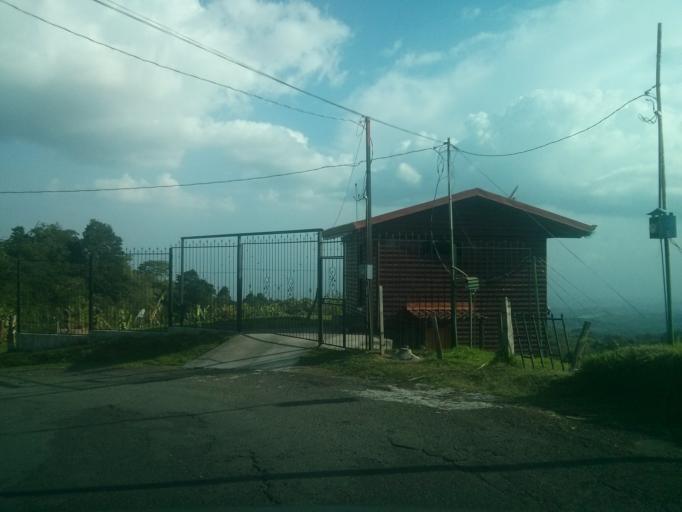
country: CR
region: Heredia
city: Santo Domingo
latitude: 10.1130
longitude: -84.1640
